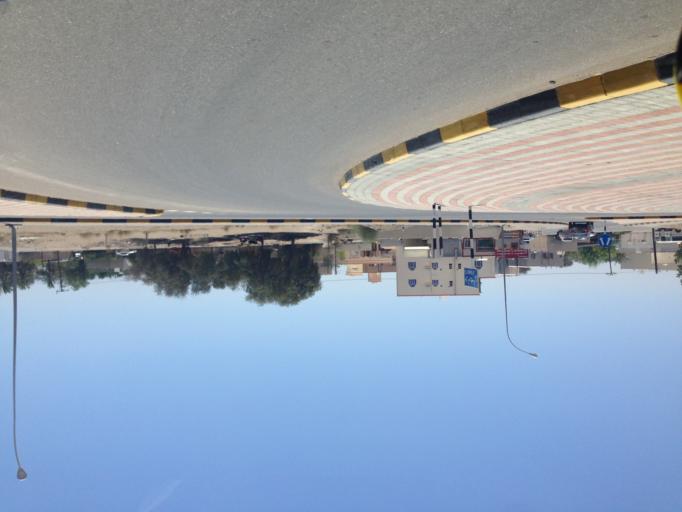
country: OM
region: Muhafazat Masqat
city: As Sib al Jadidah
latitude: 23.6567
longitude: 58.2210
